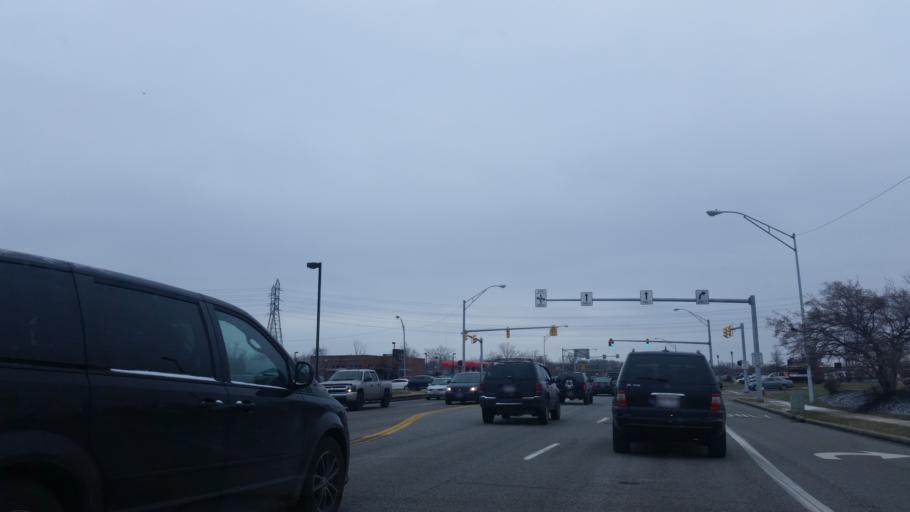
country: US
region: Ohio
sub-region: Cuyahoga County
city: Brooklyn
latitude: 41.4242
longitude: -81.7605
